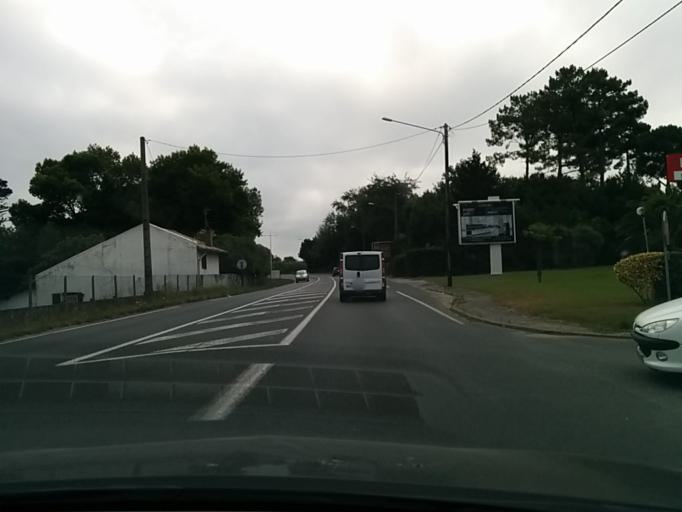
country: FR
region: Aquitaine
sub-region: Departement des Pyrenees-Atlantiques
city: Arbonne
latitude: 43.4501
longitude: -1.5620
